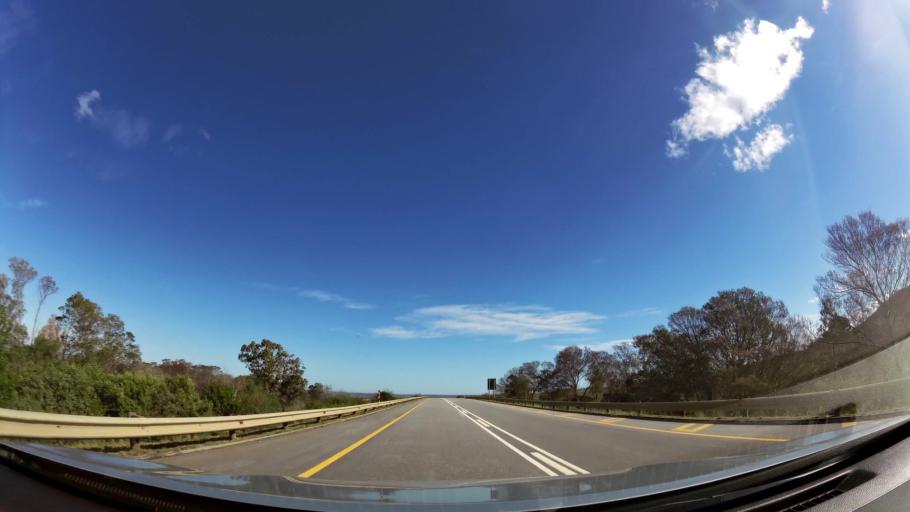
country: ZA
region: Eastern Cape
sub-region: Cacadu District Municipality
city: Kruisfontein
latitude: -33.9976
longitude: 24.6879
